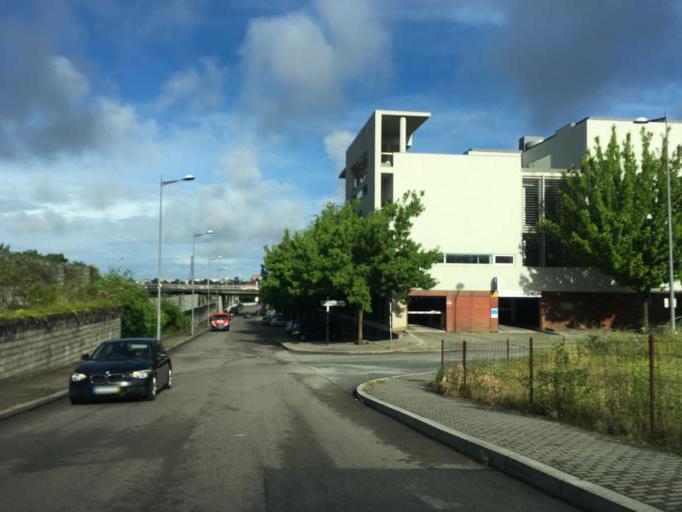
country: PT
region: Porto
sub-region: Matosinhos
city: Sao Mamede de Infesta
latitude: 41.1900
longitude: -8.6103
